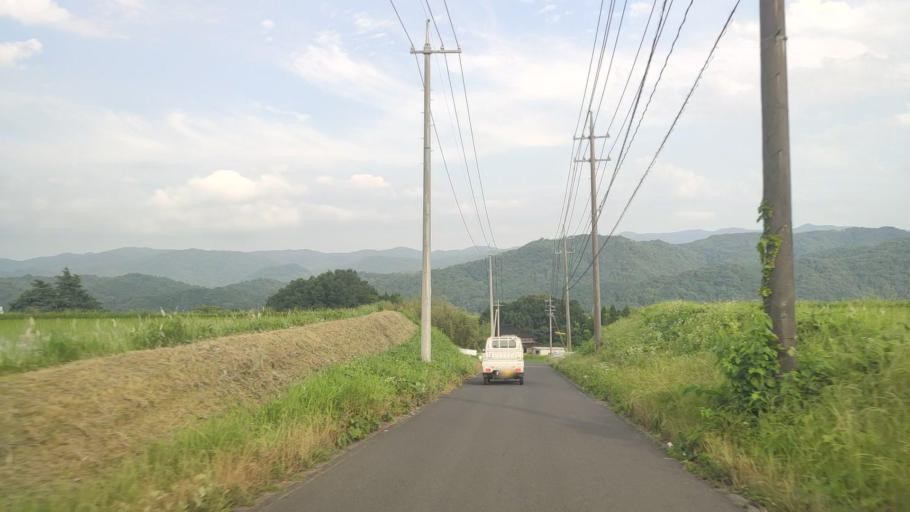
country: JP
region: Tottori
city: Kurayoshi
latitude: 35.3953
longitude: 133.7765
